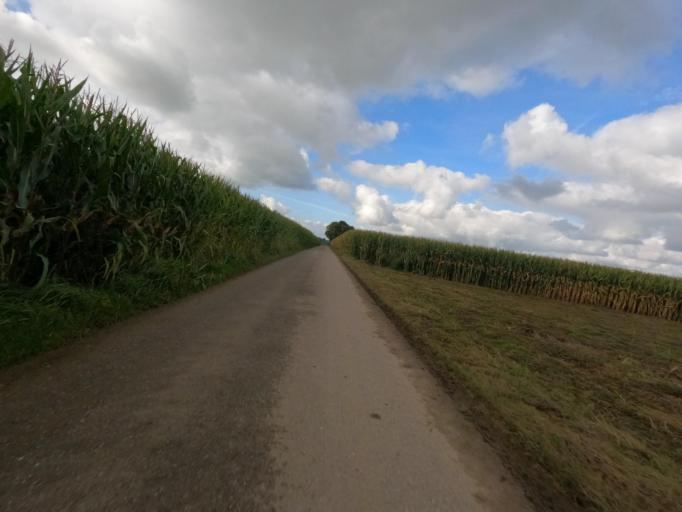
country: DE
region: North Rhine-Westphalia
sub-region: Regierungsbezirk Koln
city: Linnich
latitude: 51.0147
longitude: 6.2840
